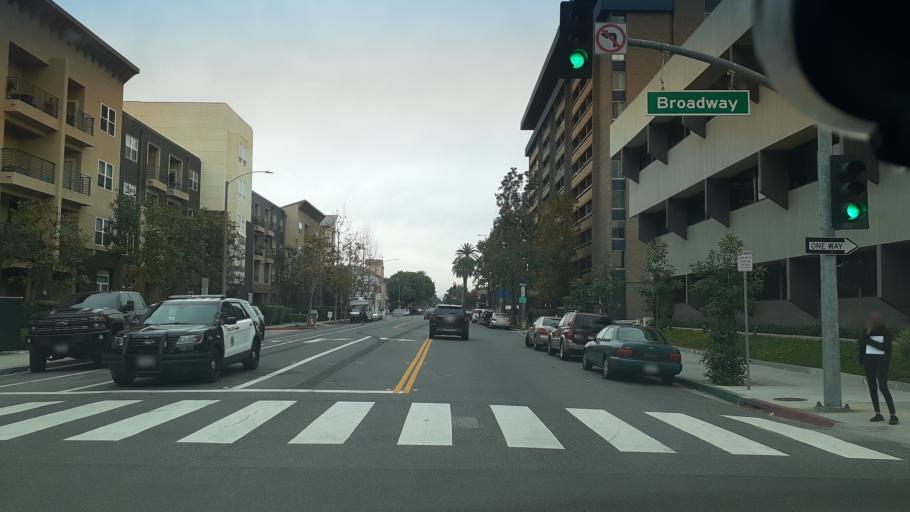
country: US
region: California
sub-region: Los Angeles County
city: Long Beach
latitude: 33.7693
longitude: -118.1963
